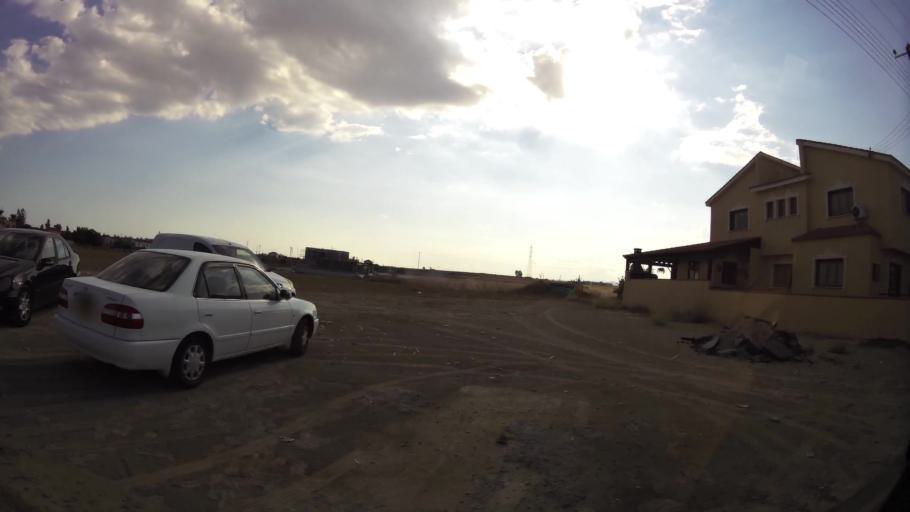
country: CY
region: Larnaka
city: Aradippou
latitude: 34.9410
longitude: 33.6075
